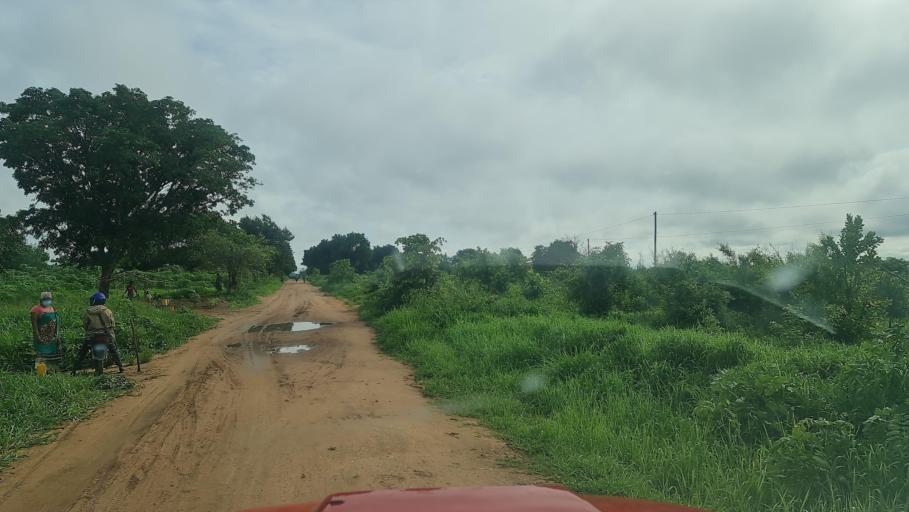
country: MW
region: Southern Region
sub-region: Nsanje District
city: Nsanje
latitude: -17.2846
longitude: 35.6107
